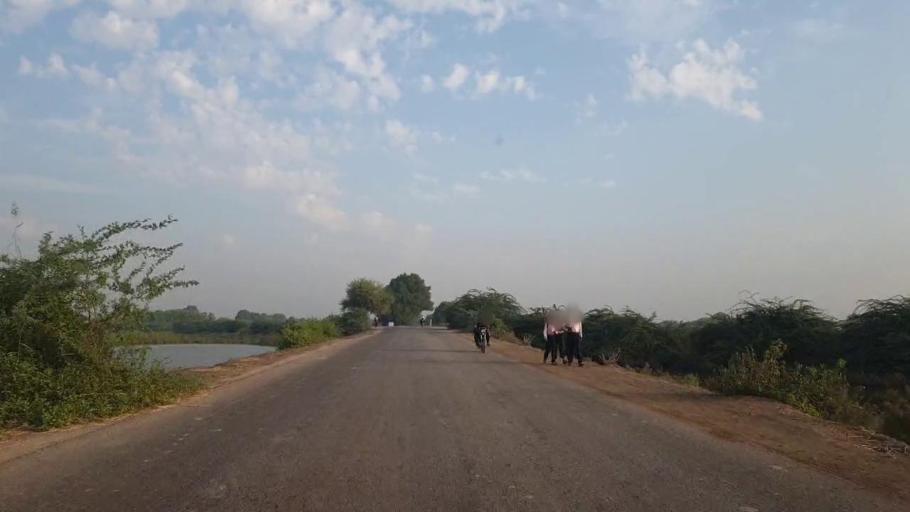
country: PK
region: Sindh
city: Tando Bago
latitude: 24.7142
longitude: 68.9391
